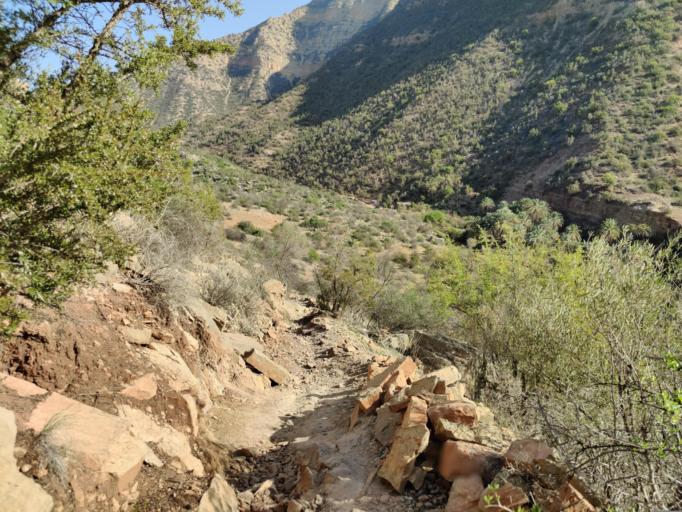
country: MA
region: Souss-Massa-Draa
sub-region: Agadir-Ida-ou-Tnan
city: Aourir
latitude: 30.5897
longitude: -9.5290
